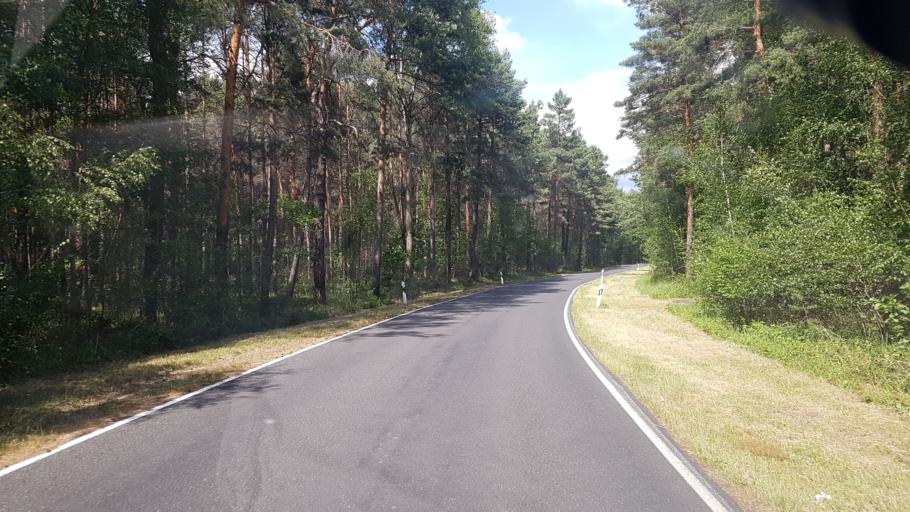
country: DE
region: Brandenburg
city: Sallgast
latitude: 51.5807
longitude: 13.9178
